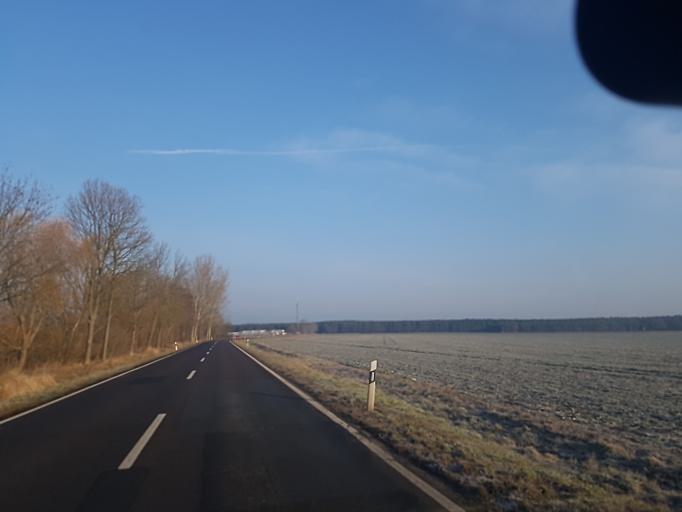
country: DE
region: Brandenburg
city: Bruck
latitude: 52.2038
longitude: 12.7519
